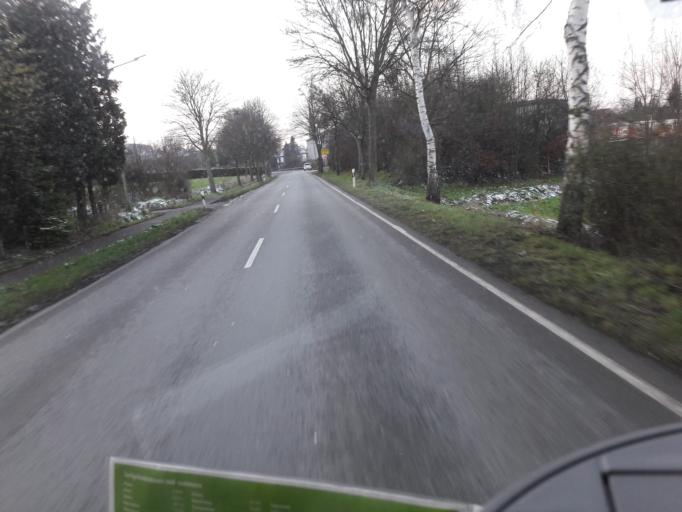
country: DE
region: Lower Saxony
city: Buckeburg
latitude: 52.2345
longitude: 9.0475
